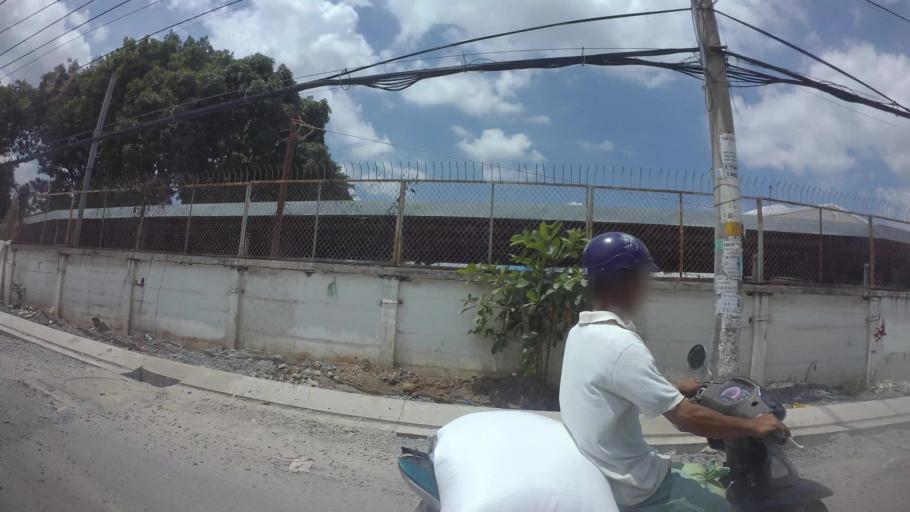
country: VN
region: Ho Chi Minh City
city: Quan Chin
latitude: 10.8317
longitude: 106.7763
